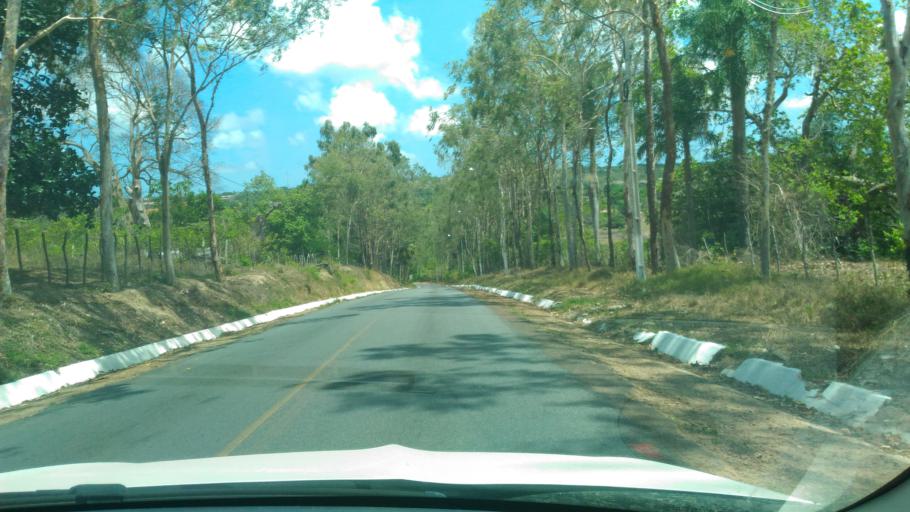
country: BR
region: Paraiba
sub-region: Conde
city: Conde
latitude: -7.2627
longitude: -34.9276
